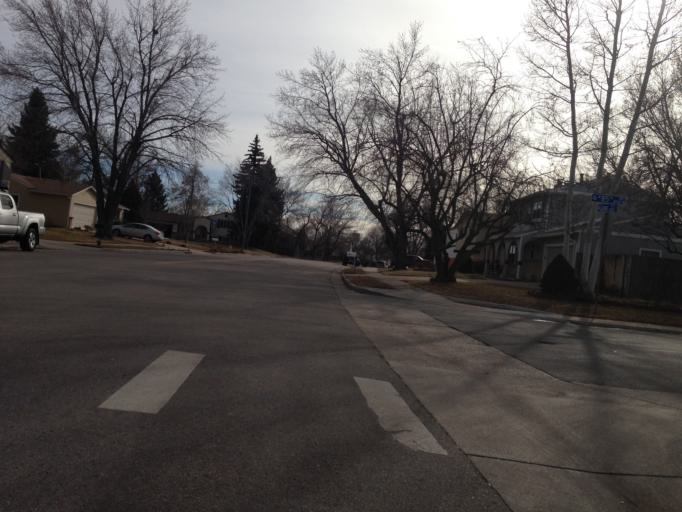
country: US
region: Colorado
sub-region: Adams County
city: Westminster
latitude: 39.8521
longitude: -105.0643
